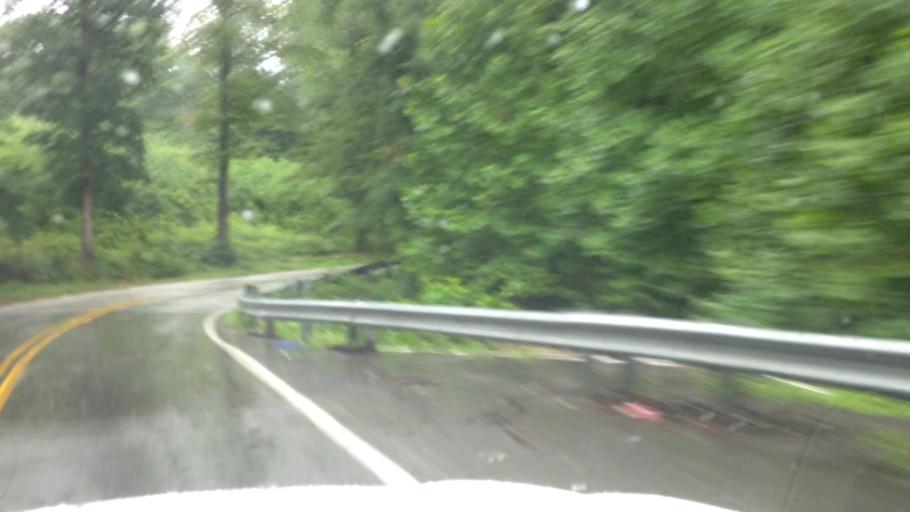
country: US
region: Maryland
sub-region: Anne Arundel County
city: Odenton
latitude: 39.1029
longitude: -76.6919
